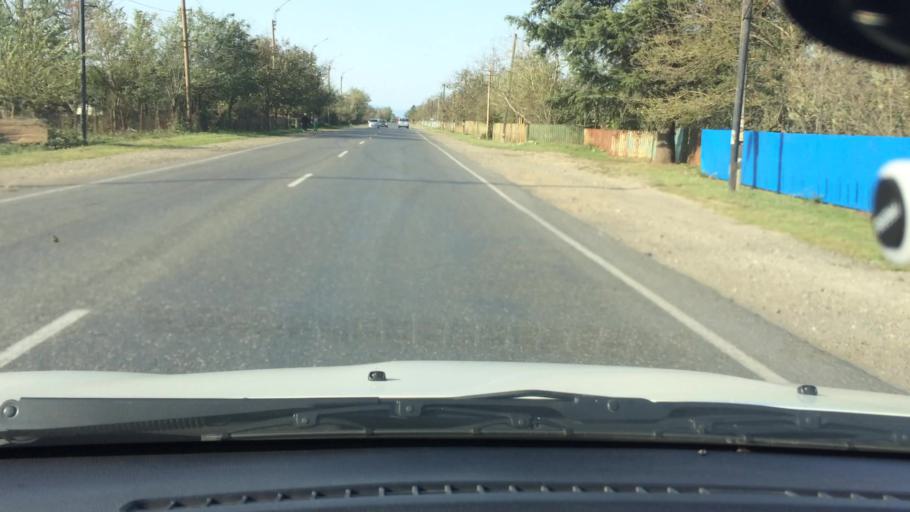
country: GE
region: Imereti
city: Kutaisi
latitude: 42.2425
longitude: 42.6325
